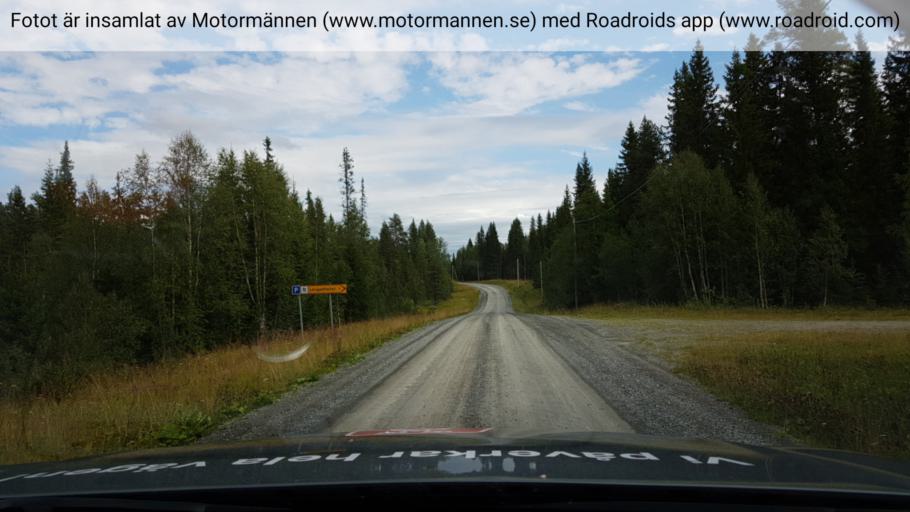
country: SE
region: Jaemtland
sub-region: Krokoms Kommun
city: Valla
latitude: 63.7121
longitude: 13.5364
